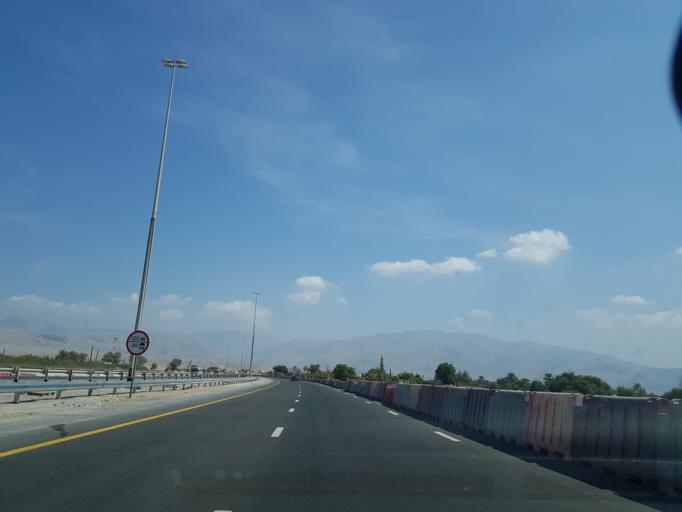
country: AE
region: Ra's al Khaymah
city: Ras al-Khaimah
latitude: 25.6972
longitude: 55.9798
